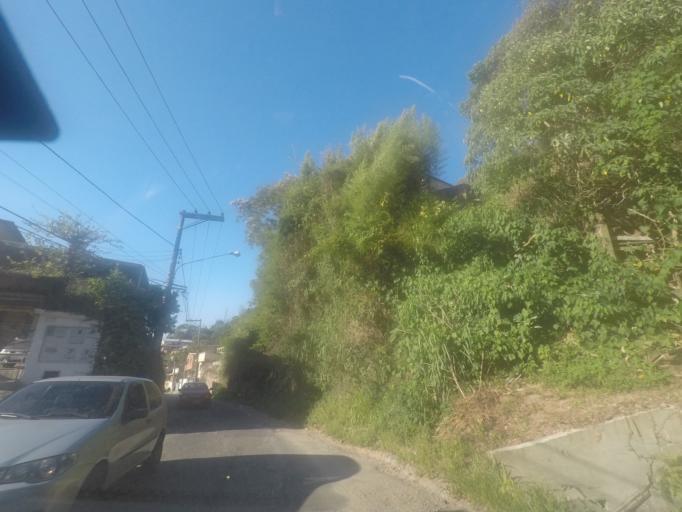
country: BR
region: Rio de Janeiro
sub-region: Petropolis
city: Petropolis
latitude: -22.4951
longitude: -43.1490
